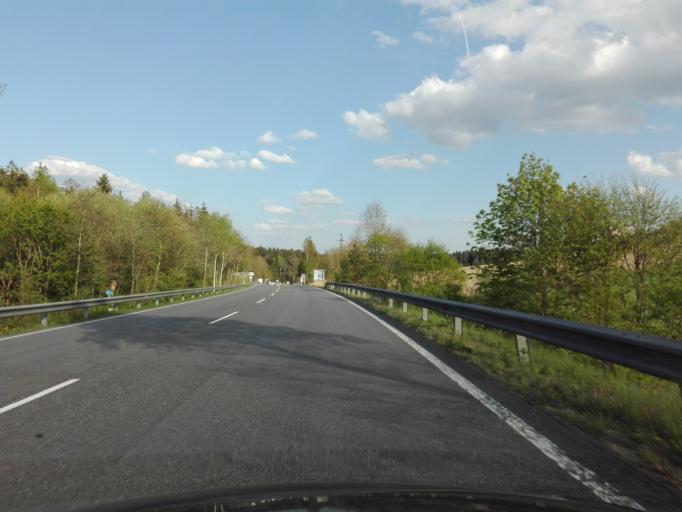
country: AT
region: Upper Austria
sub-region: Politischer Bezirk Rohrbach
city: Kleinzell im Muehlkreis
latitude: 48.4649
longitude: 14.0201
